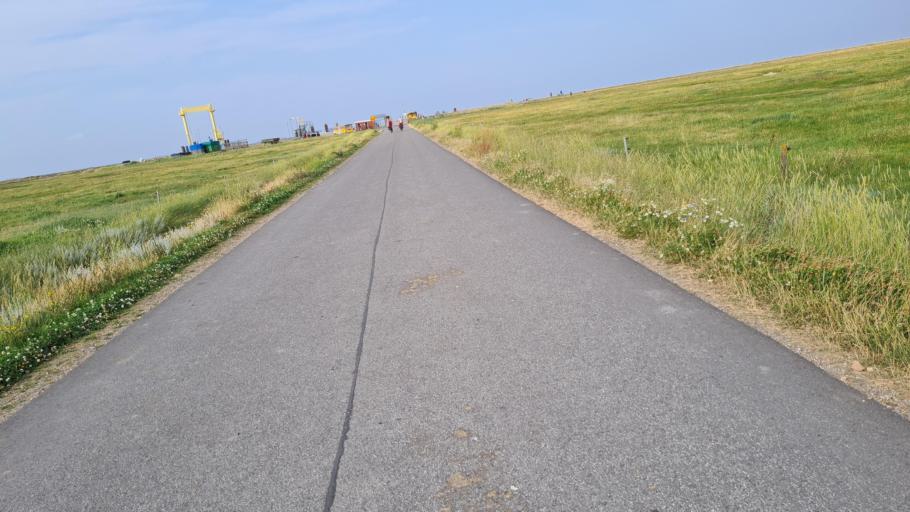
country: DE
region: Schleswig-Holstein
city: Hooge
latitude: 54.5766
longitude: 8.5546
